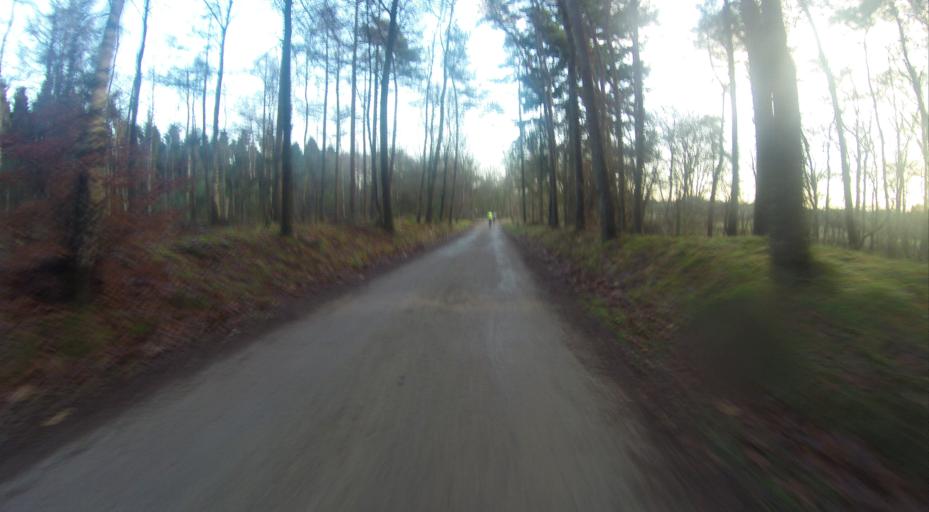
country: NL
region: Overijssel
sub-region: Gemeente Hof van Twente
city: Markelo
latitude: 52.2930
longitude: 6.4297
